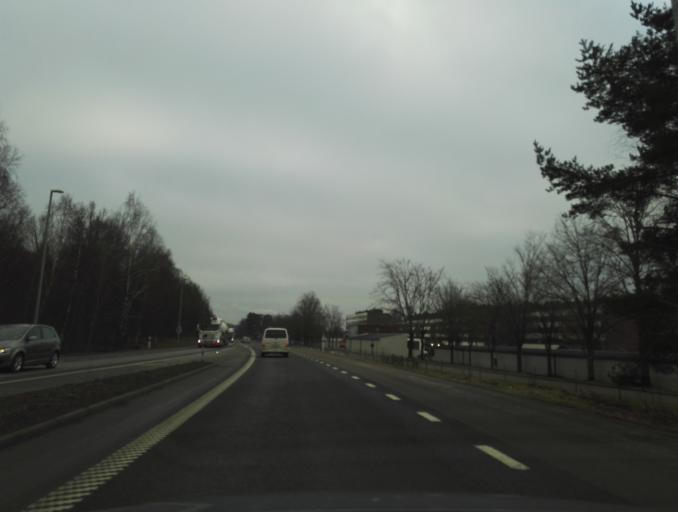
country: SE
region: Kronoberg
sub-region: Vaxjo Kommun
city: Vaexjoe
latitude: 56.8866
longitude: 14.8281
